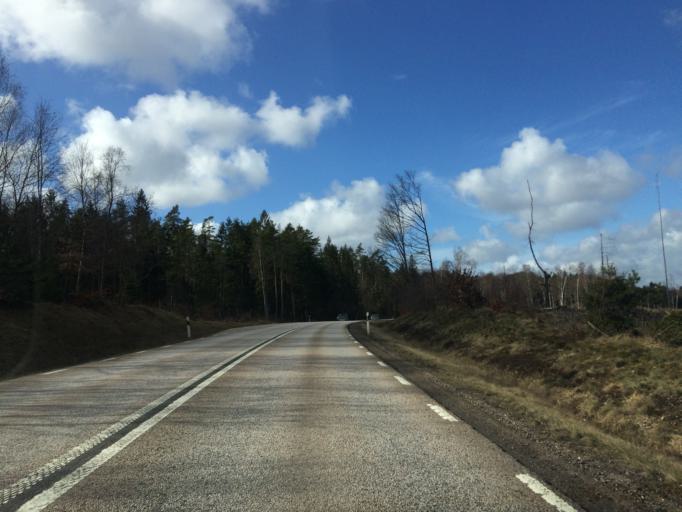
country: SE
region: Kronoberg
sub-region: Markaryds Kommun
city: Markaryd
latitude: 56.4761
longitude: 13.4949
